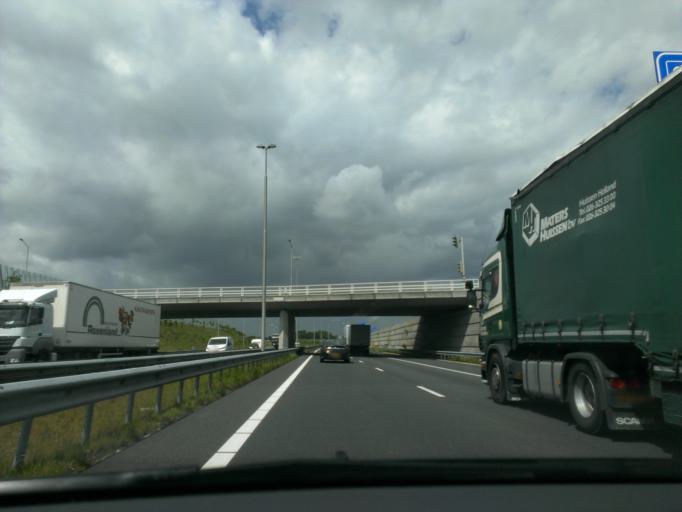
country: NL
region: Limburg
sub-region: Gemeente Venlo
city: Tegelen
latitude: 51.3613
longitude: 6.1328
